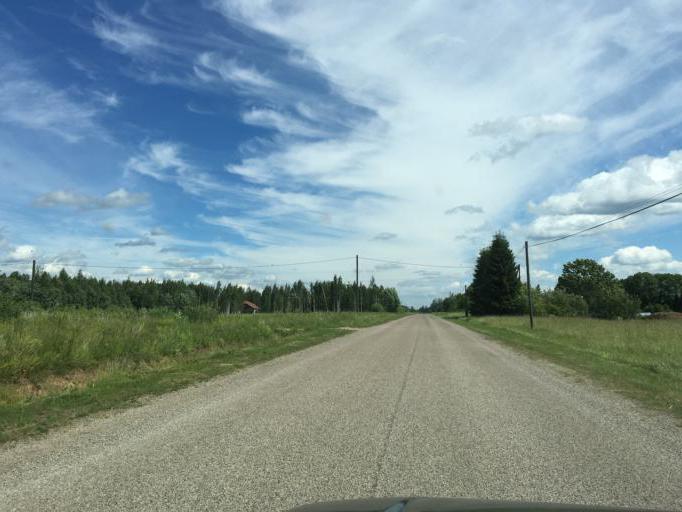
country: LV
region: Balvu Rajons
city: Balvi
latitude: 57.1412
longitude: 27.2793
